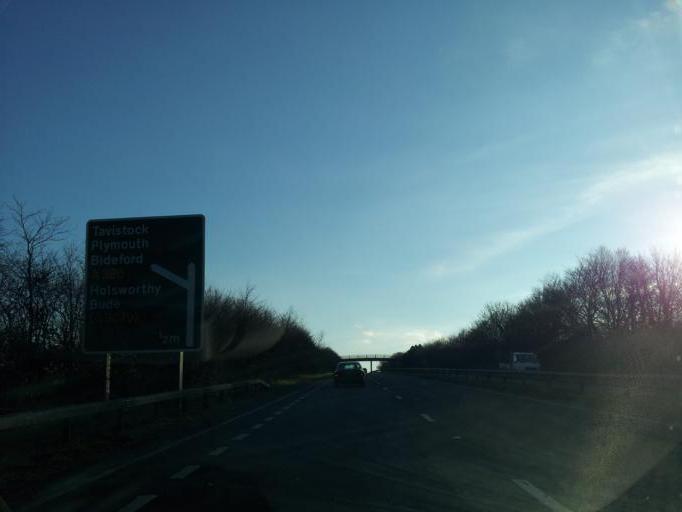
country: GB
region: England
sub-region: Devon
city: Okehampton
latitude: 50.7131
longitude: -4.0505
